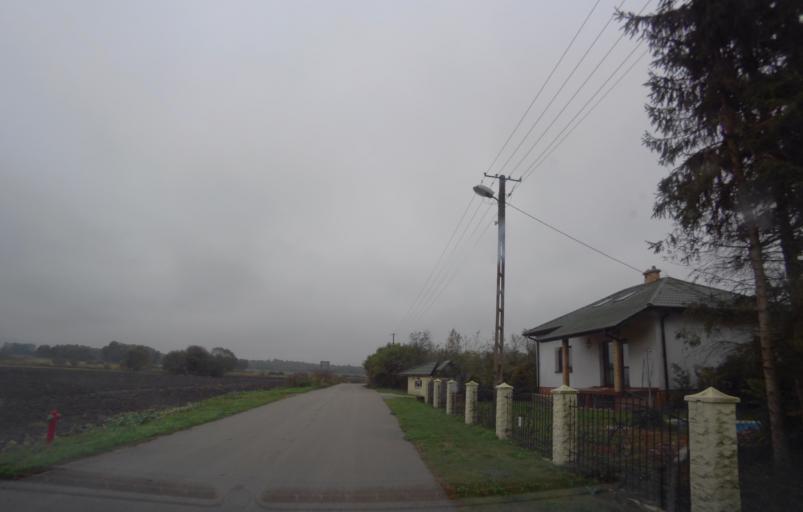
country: PL
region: Lublin Voivodeship
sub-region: Chelm
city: Chelm
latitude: 51.2099
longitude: 23.4583
